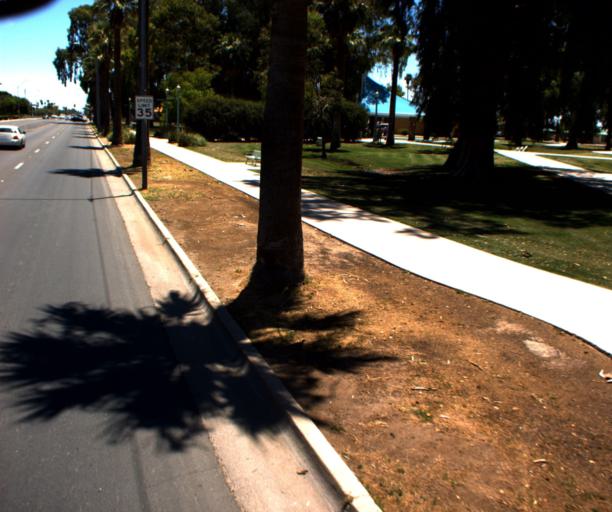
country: US
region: Arizona
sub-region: Pinal County
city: Casa Grande
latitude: 32.8795
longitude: -111.7504
